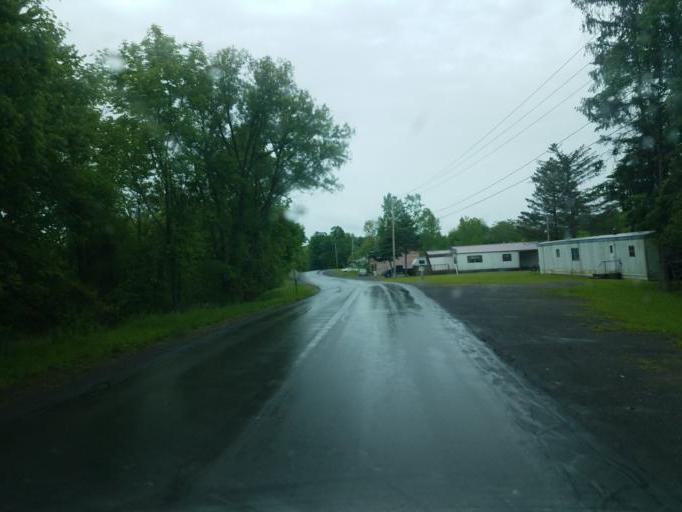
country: US
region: New York
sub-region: Herkimer County
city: Ilion
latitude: 43.0023
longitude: -75.0240
